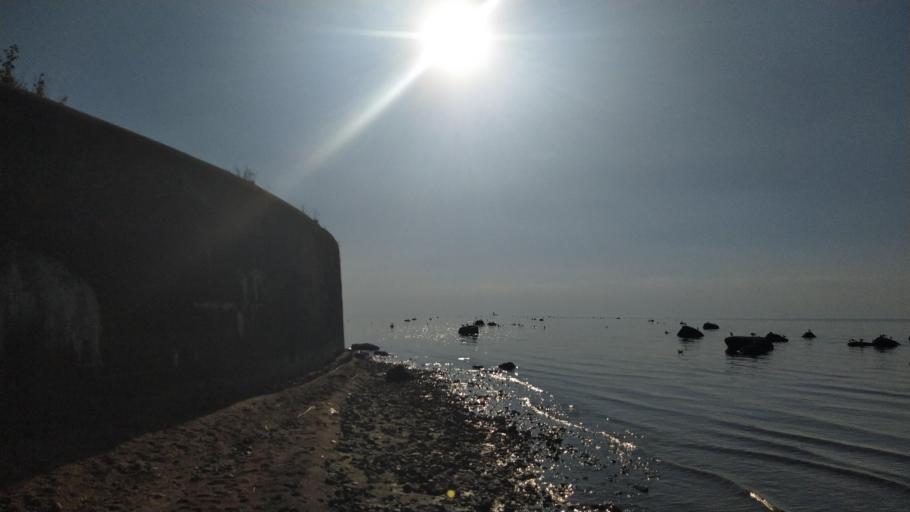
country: RU
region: St.-Petersburg
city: Bol'shaya Izhora
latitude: 60.0336
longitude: 29.6390
